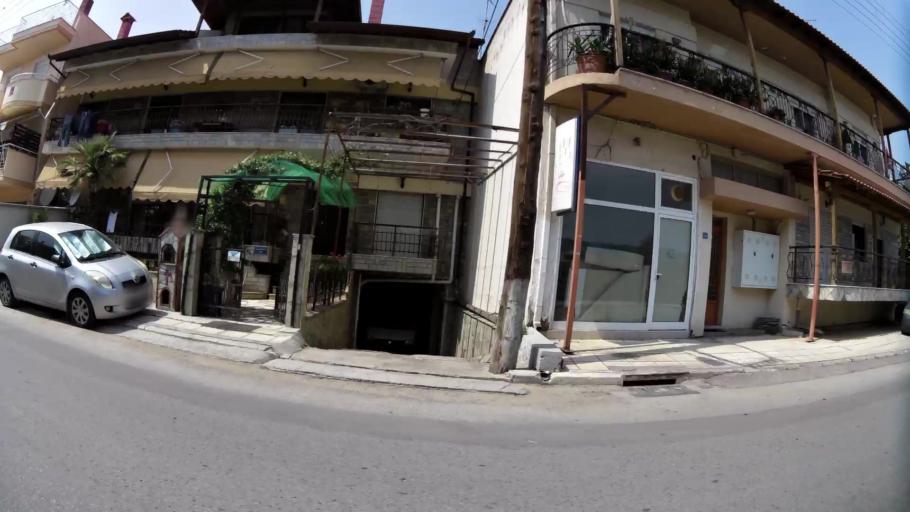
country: GR
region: Central Macedonia
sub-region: Nomos Thessalonikis
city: Nea Magnisia
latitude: 40.6865
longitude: 22.8511
